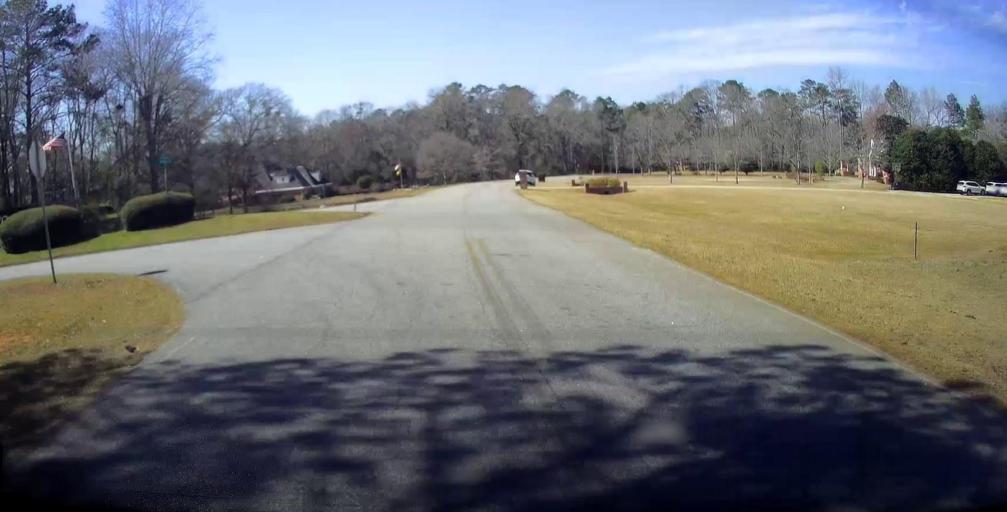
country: US
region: Georgia
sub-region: Houston County
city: Perry
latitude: 32.4473
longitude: -83.6994
